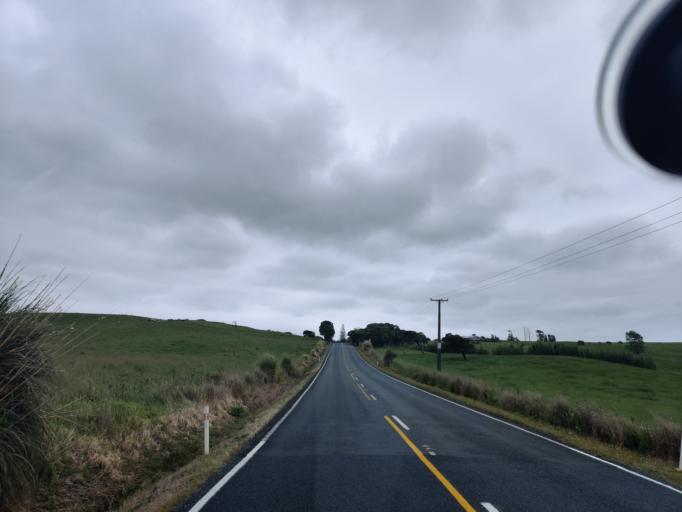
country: NZ
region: Northland
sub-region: Kaipara District
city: Dargaville
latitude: -36.1248
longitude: 174.1137
